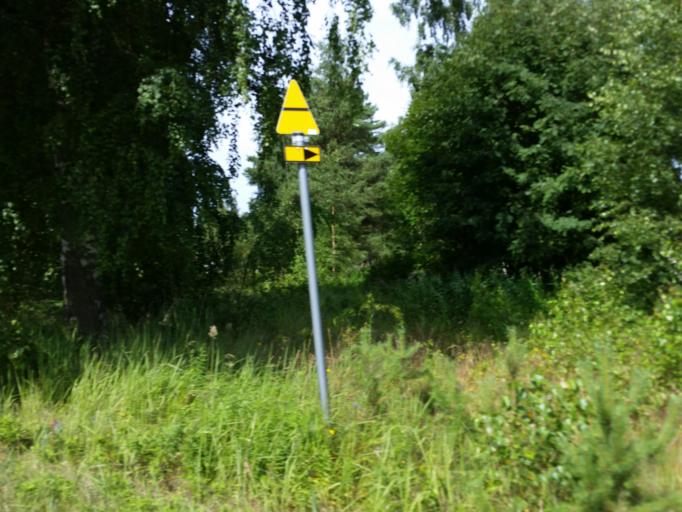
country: FI
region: Uusimaa
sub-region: Raaseporin
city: Hanko
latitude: 59.8254
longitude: 22.9326
